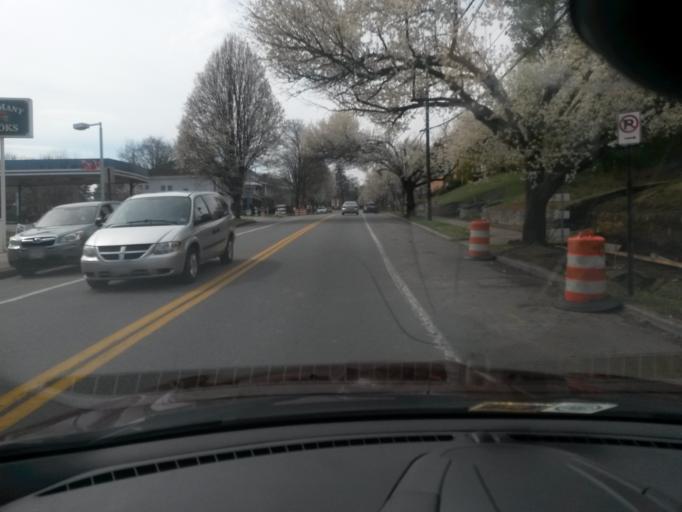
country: US
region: Virginia
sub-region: City of Roanoke
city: Roanoke
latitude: 37.2635
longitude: -79.9777
